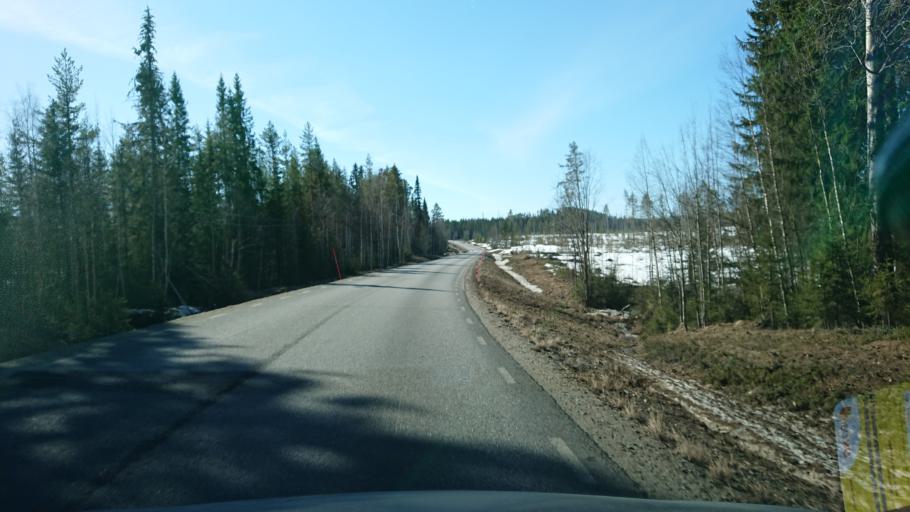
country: SE
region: Vaesterbotten
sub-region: Dorotea Kommun
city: Dorotea
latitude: 64.0839
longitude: 16.2609
